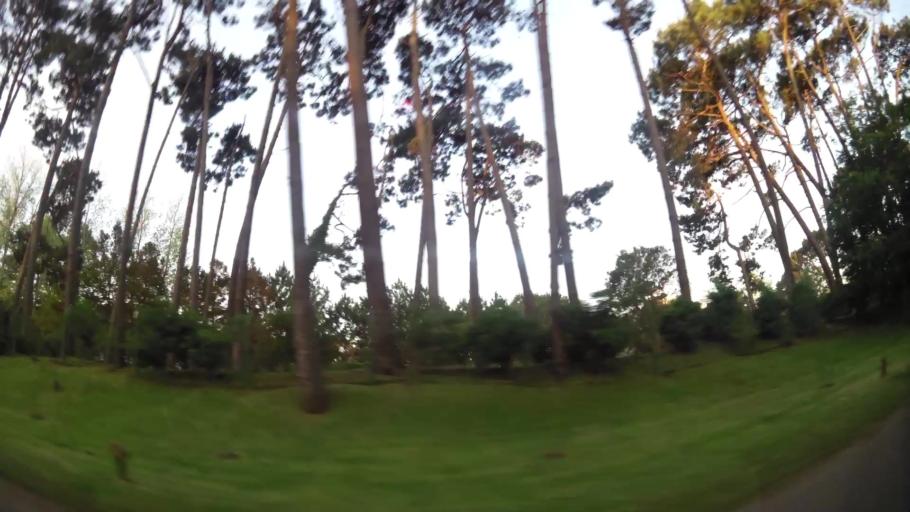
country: UY
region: Maldonado
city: Maldonado
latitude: -34.9329
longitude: -54.9333
